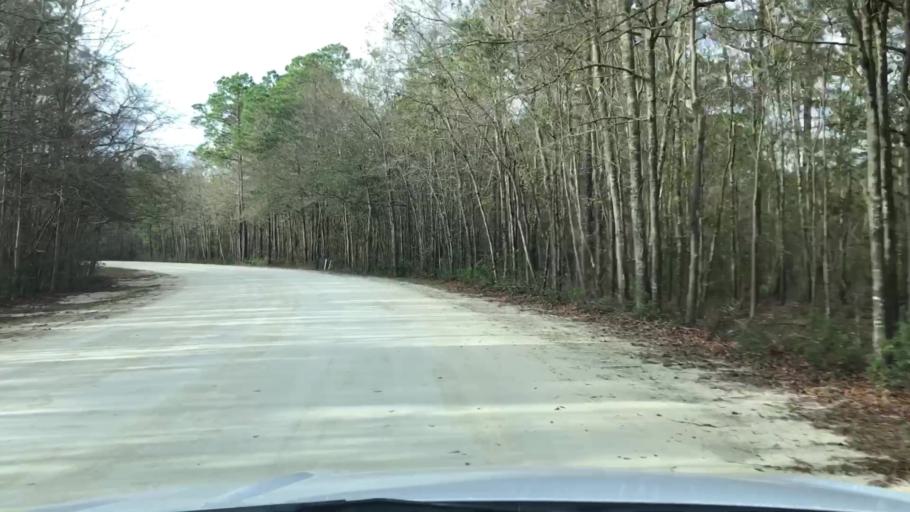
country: US
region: South Carolina
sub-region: Charleston County
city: Isle of Palms
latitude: 32.9022
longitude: -79.7256
